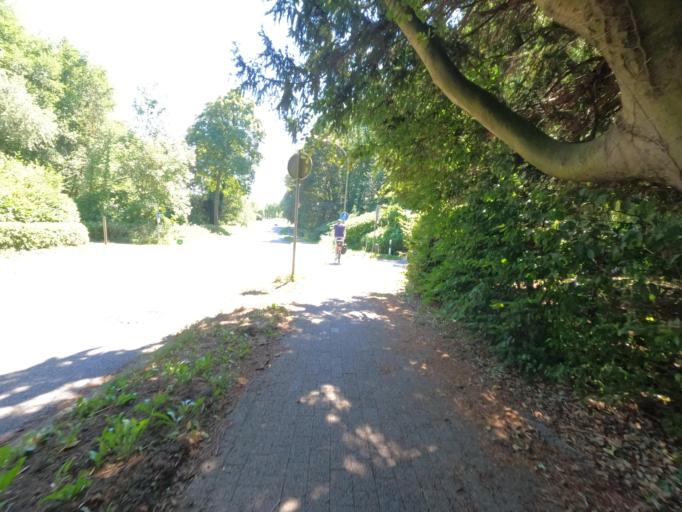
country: DE
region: North Rhine-Westphalia
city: Wegberg
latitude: 51.1546
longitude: 6.2692
